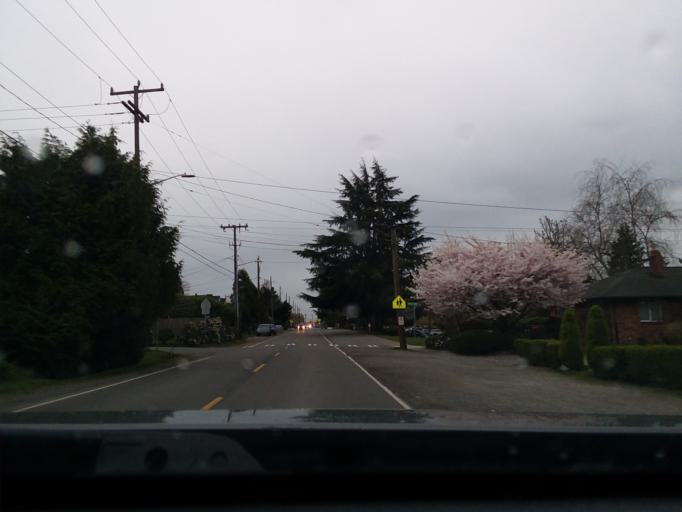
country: US
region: Washington
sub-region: King County
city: Shoreline
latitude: 47.6982
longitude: -122.3768
